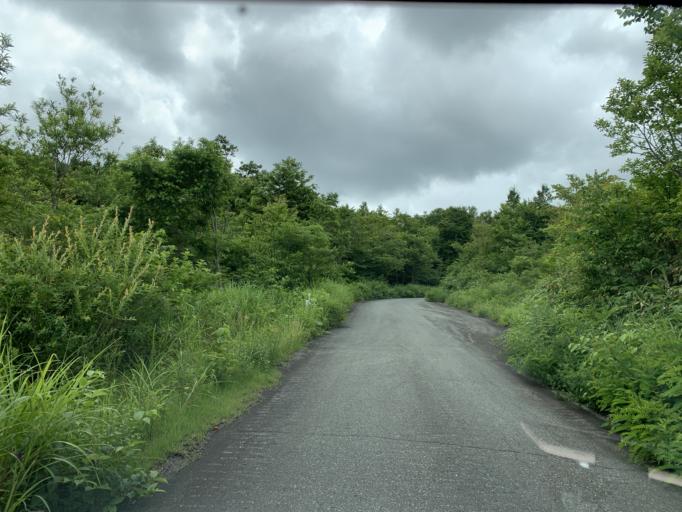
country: JP
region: Iwate
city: Ichinoseki
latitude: 38.9340
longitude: 140.8821
